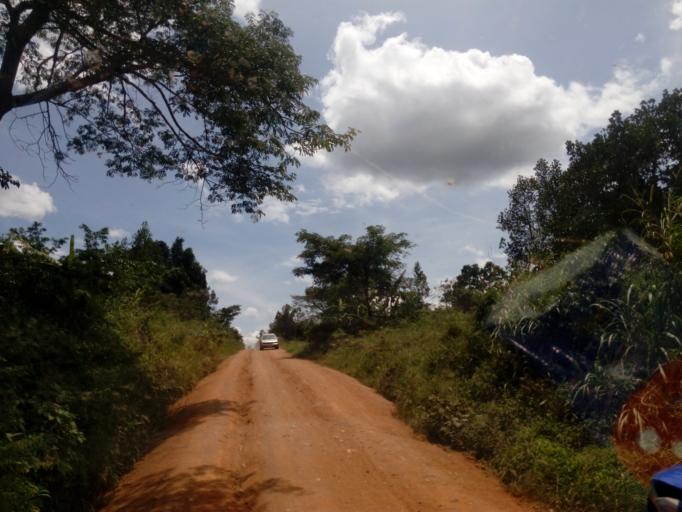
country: UG
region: Central Region
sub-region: Mubende District
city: Mubende
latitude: 0.4616
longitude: 31.7022
